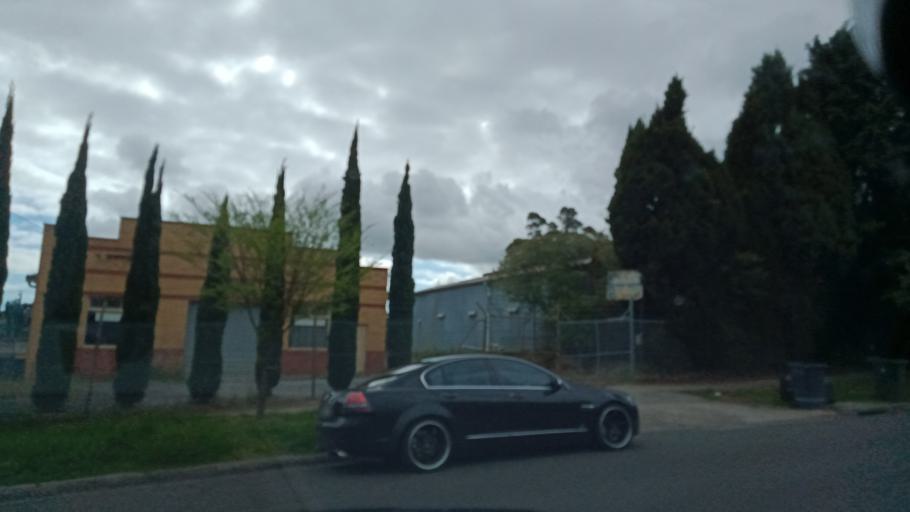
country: AU
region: Victoria
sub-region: Monash
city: Notting Hill
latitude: -37.8853
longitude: 145.1600
